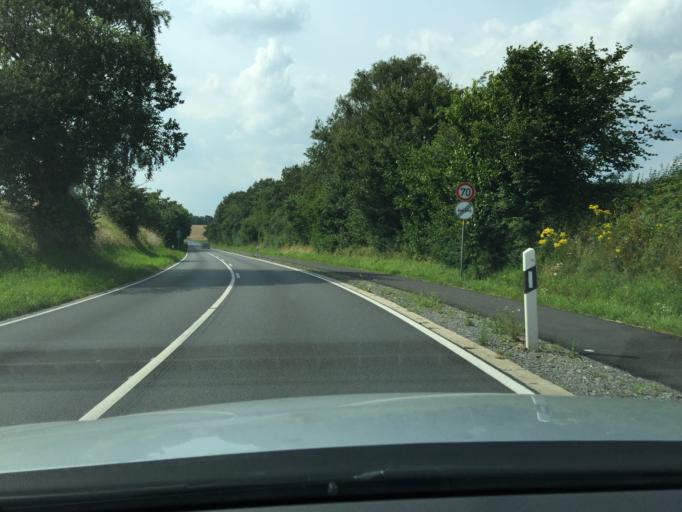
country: DE
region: North Rhine-Westphalia
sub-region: Regierungsbezirk Dusseldorf
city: Velbert
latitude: 51.3578
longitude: 7.0831
